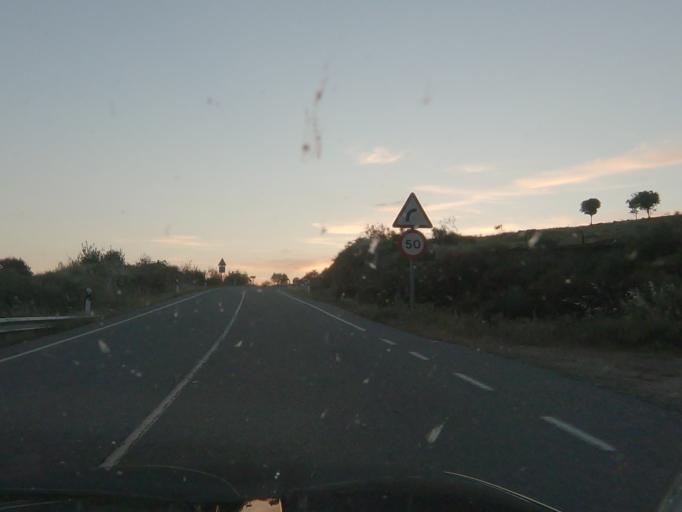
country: ES
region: Extremadura
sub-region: Provincia de Caceres
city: Alcantara
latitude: 39.7343
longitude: -6.9064
